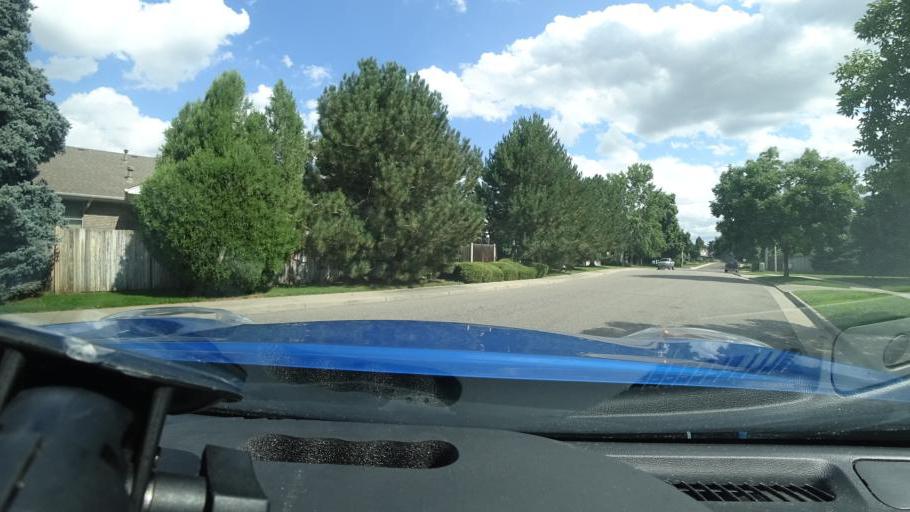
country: US
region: Colorado
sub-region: Adams County
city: Aurora
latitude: 39.6935
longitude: -104.8589
